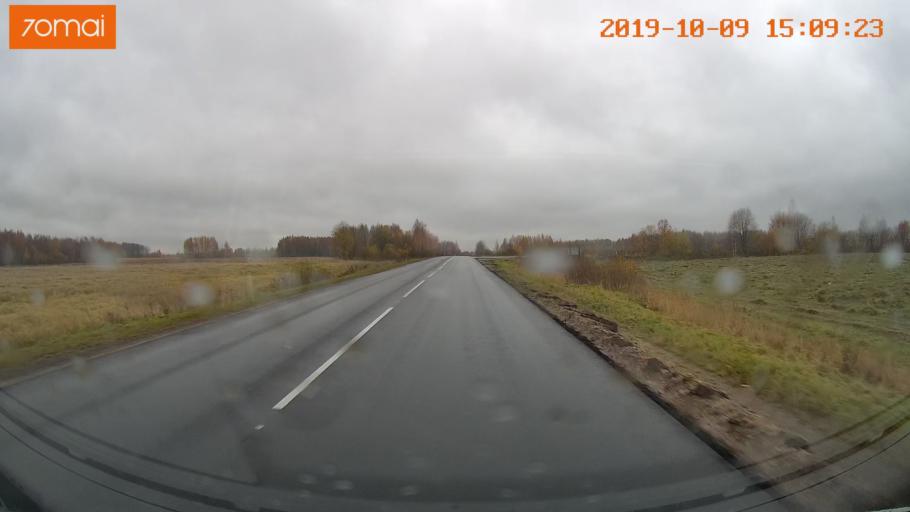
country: RU
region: Kostroma
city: Susanino
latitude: 58.1922
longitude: 41.6505
